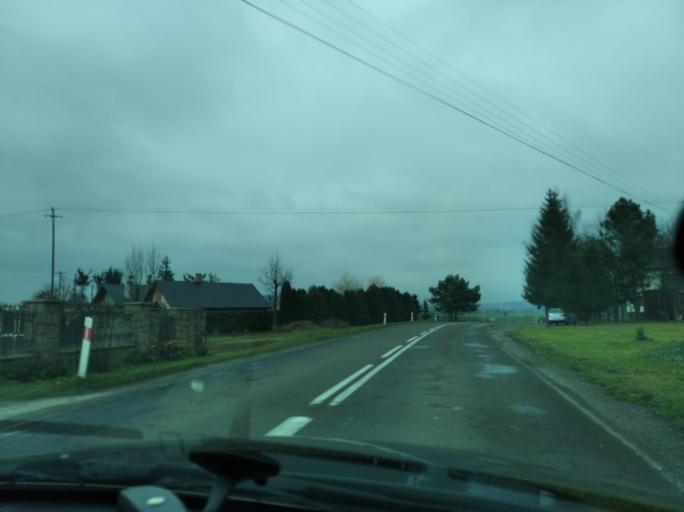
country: PL
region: Subcarpathian Voivodeship
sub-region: Powiat rzeszowski
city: Dynow
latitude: 49.8452
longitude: 22.2436
